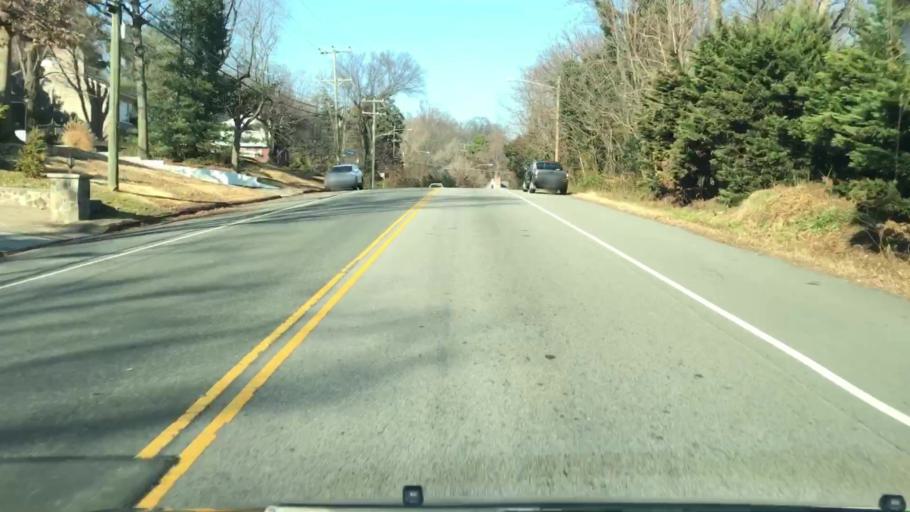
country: US
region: Virginia
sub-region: Fairfax County
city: Belle Haven
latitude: 38.7782
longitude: -77.0629
